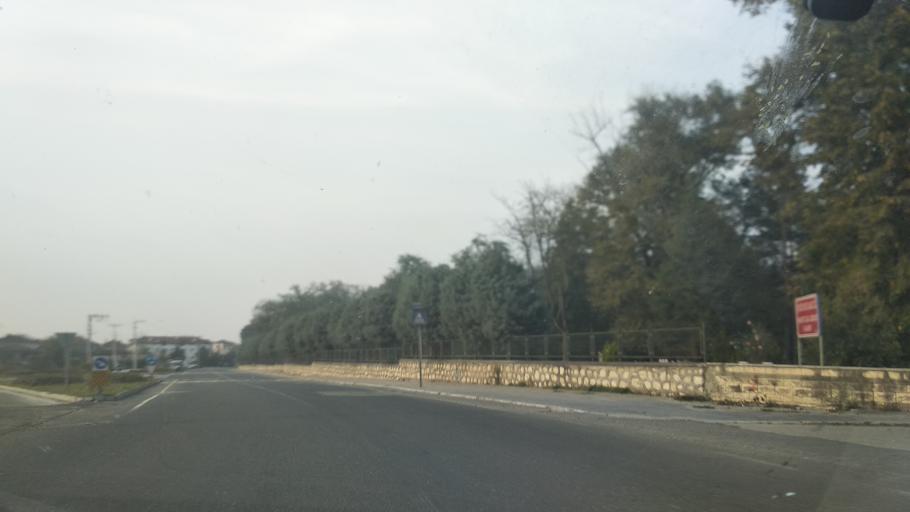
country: TR
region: Duzce
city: Duzce
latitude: 40.8262
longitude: 31.1745
